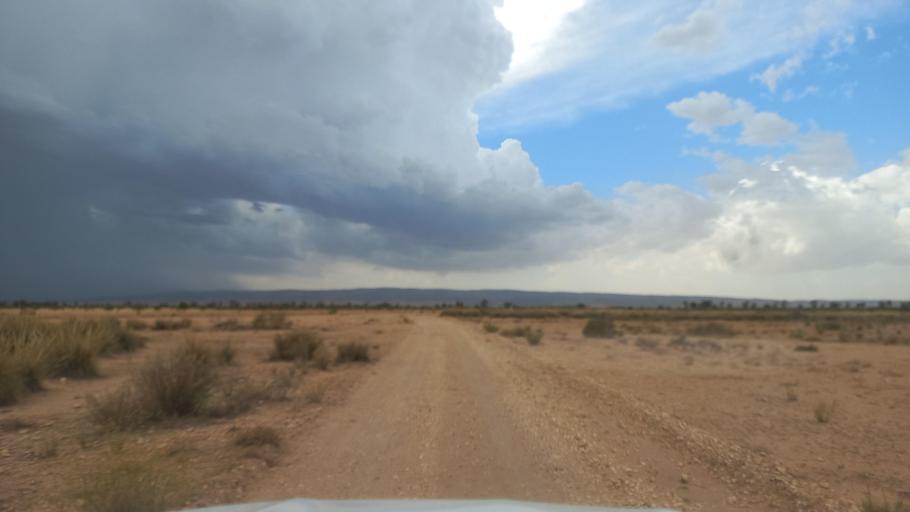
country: TN
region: Al Qasrayn
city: Kasserine
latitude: 35.2419
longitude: 9.0097
